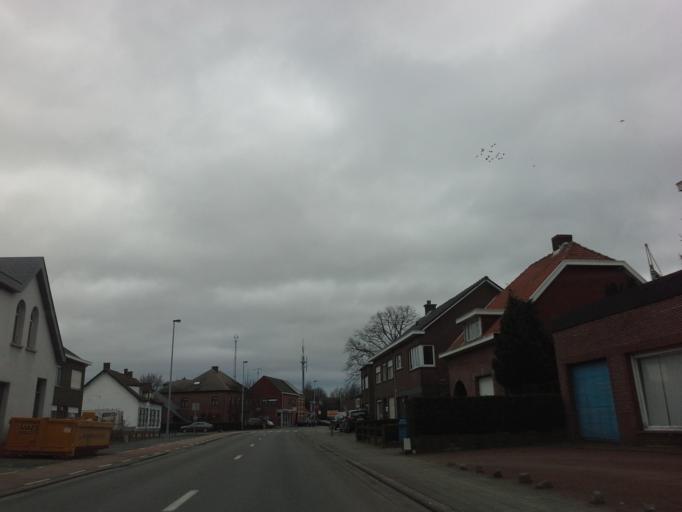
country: BE
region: Flanders
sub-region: Provincie Antwerpen
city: Olen
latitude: 51.1245
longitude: 4.8260
